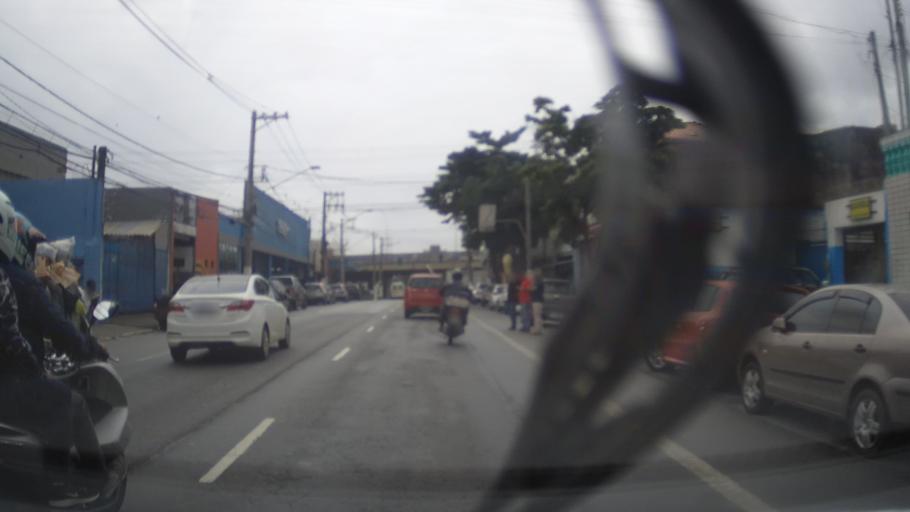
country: BR
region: Sao Paulo
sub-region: Guarulhos
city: Guarulhos
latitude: -23.4600
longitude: -46.5730
